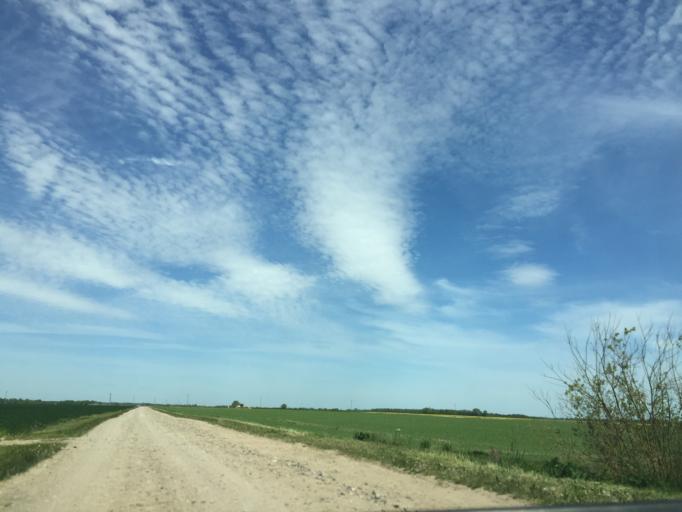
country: LT
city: Linkuva
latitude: 56.0516
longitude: 24.0936
